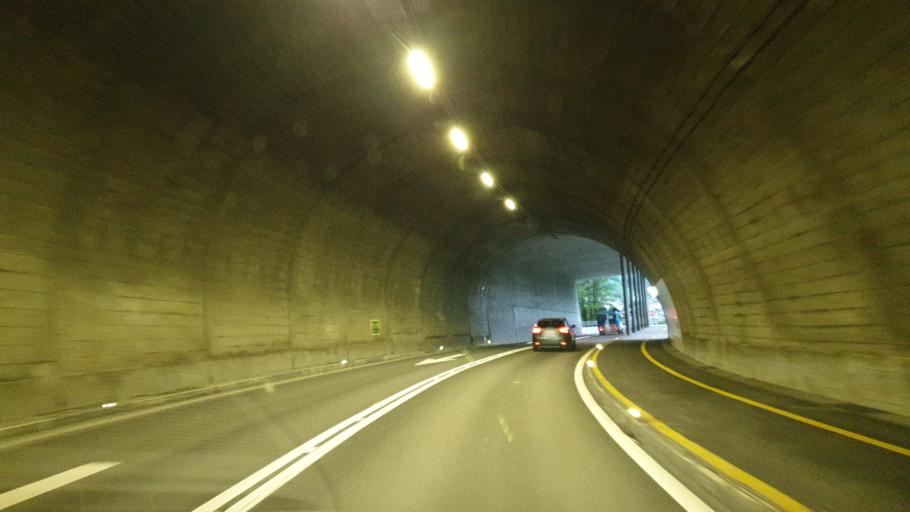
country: CH
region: Uri
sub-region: Uri
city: Flueelen
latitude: 46.9220
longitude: 8.6208
